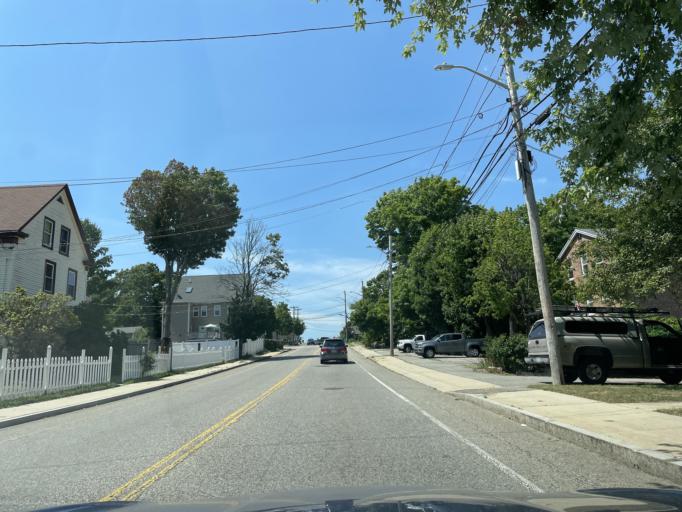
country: US
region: Massachusetts
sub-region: Norfolk County
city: Randolph
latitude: 42.1612
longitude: -71.0391
